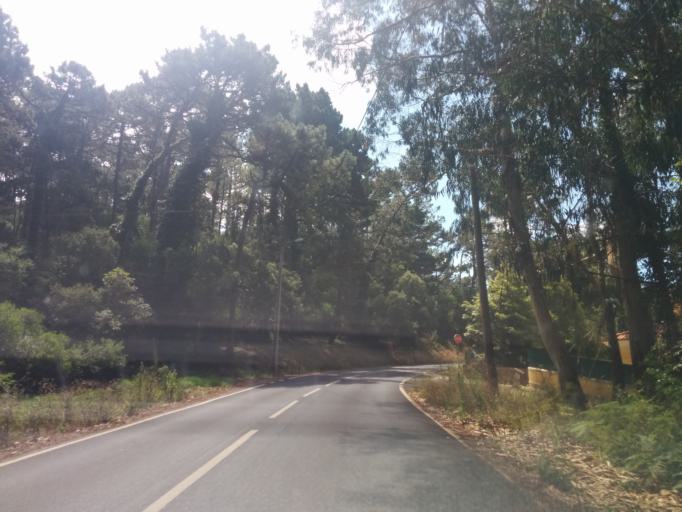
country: PT
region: Lisbon
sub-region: Sintra
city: Colares
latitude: 38.7763
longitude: -9.4751
